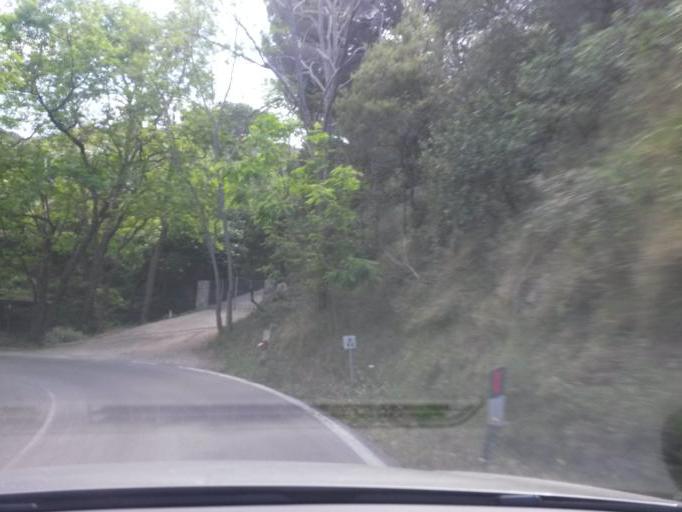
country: IT
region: Tuscany
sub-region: Provincia di Livorno
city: Marciana Marina
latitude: 42.7919
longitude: 10.2200
